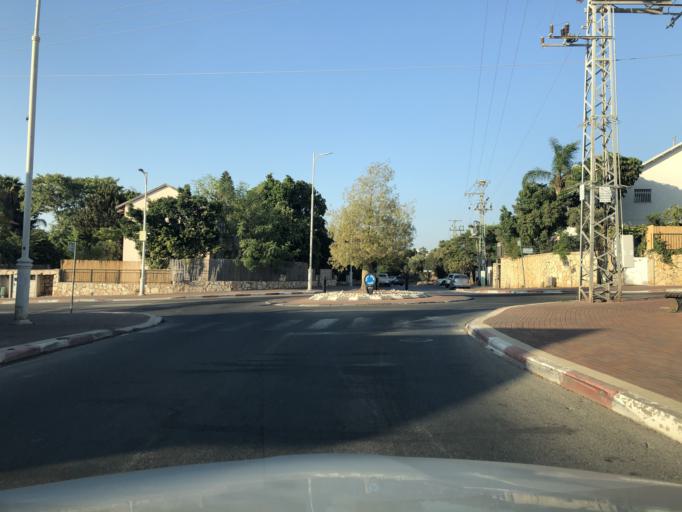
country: PS
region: West Bank
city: Hablah
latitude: 32.1624
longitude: 34.9724
